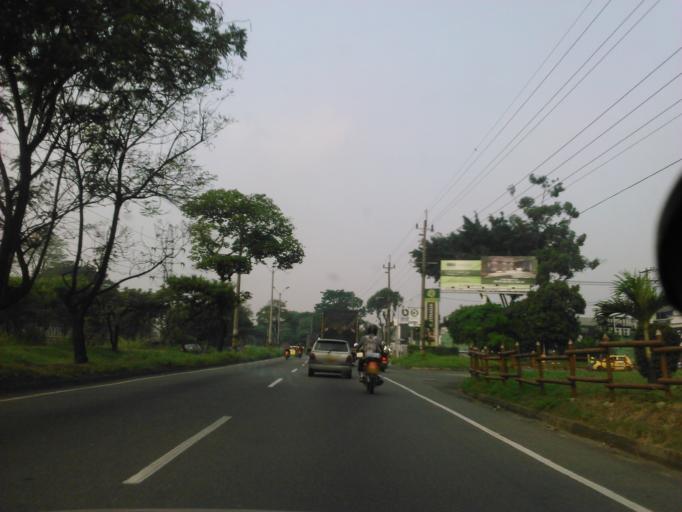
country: CO
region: Antioquia
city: Envigado
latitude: 6.1861
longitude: -75.5870
